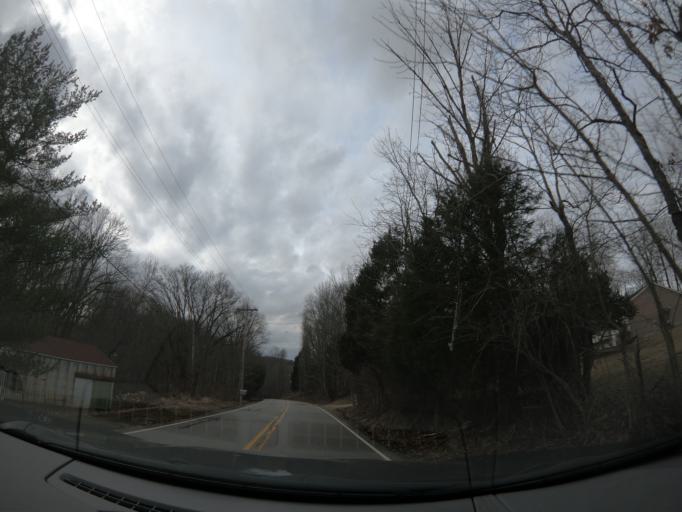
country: US
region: Indiana
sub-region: Floyd County
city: Galena
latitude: 38.3900
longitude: -85.9083
